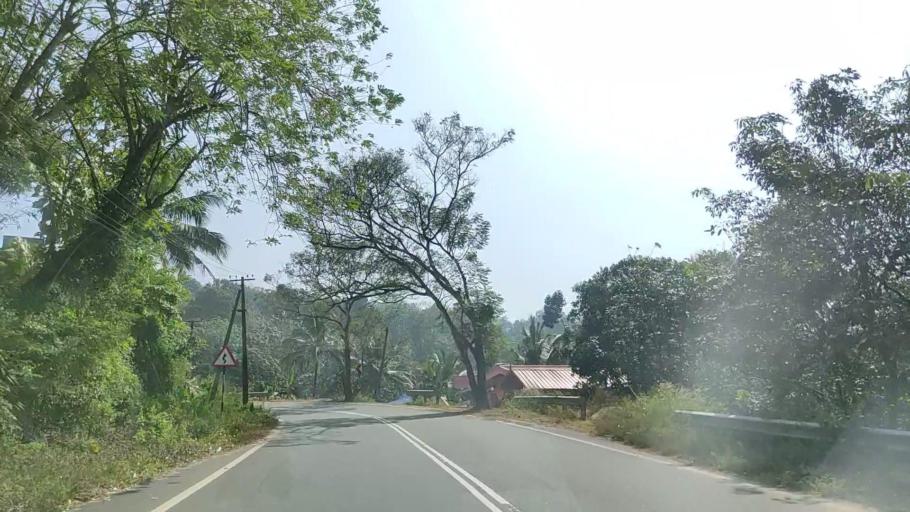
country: IN
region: Kerala
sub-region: Kollam
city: Punalur
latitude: 8.9303
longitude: 76.9942
